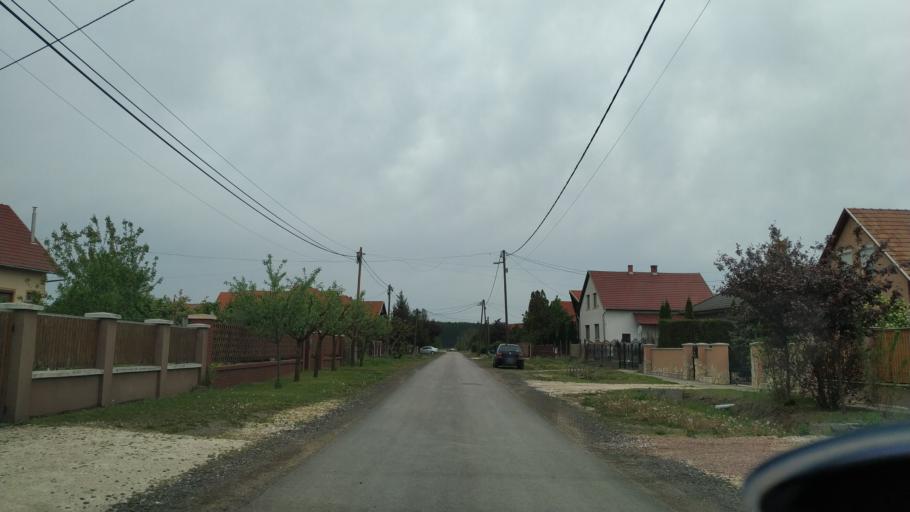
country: HU
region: Pest
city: Nagykata
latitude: 47.4216
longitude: 19.7249
